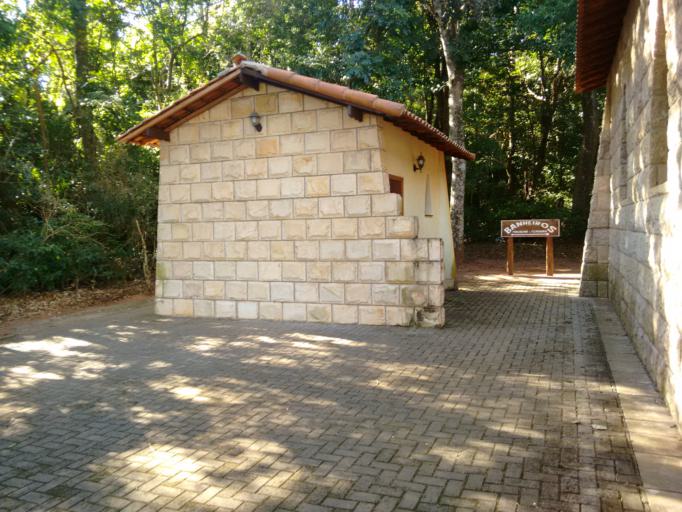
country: BR
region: Sao Paulo
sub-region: Sao Carlos
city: Sao Carlos
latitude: -21.9607
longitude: -47.8957
